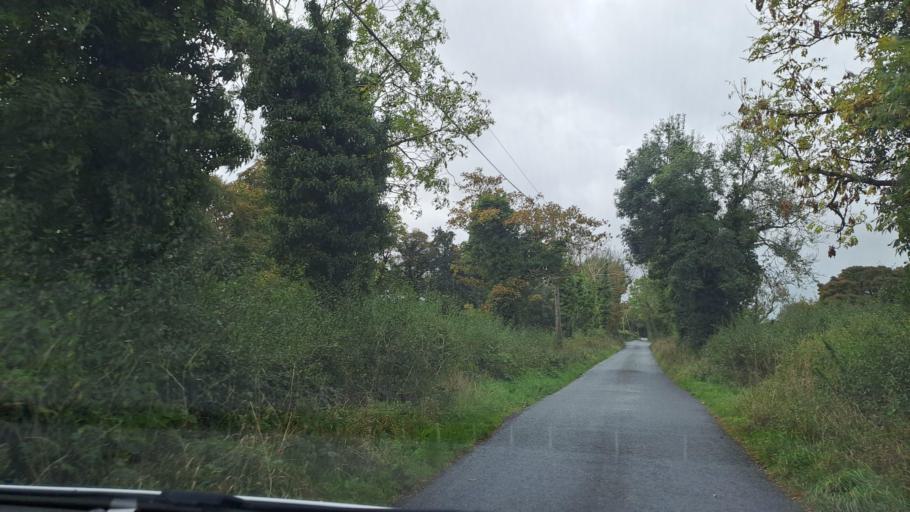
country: IE
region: Ulster
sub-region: An Cabhan
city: Kingscourt
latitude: 53.9460
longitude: -6.8311
